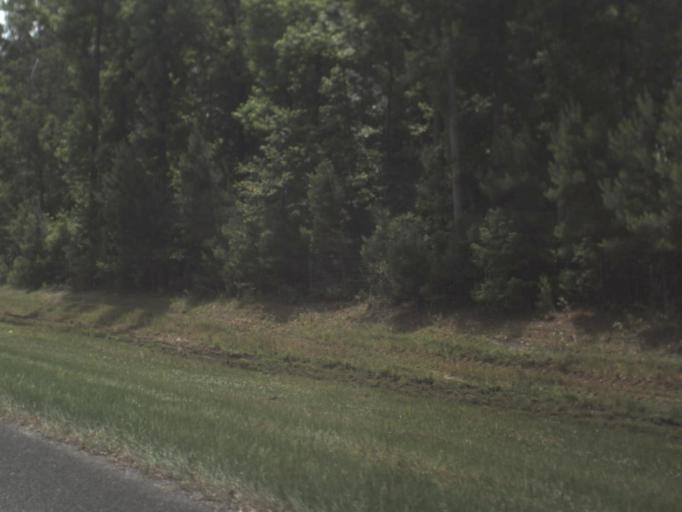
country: US
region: Florida
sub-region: Nassau County
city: Yulee
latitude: 30.6154
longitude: -81.7061
